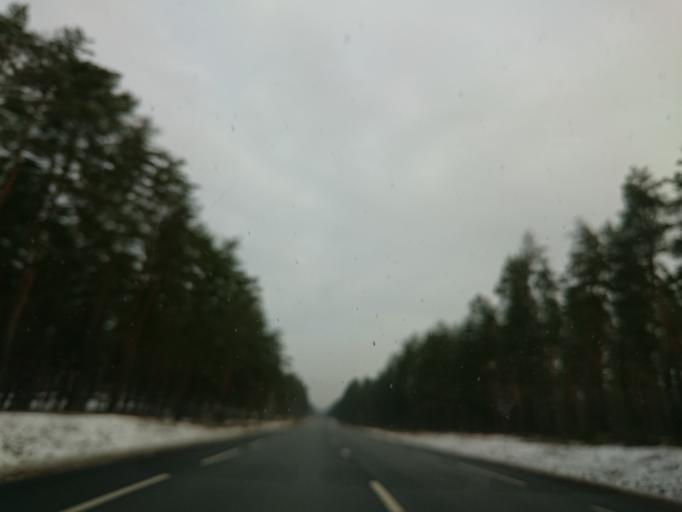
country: LV
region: Carnikava
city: Carnikava
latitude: 57.1651
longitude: 24.3449
